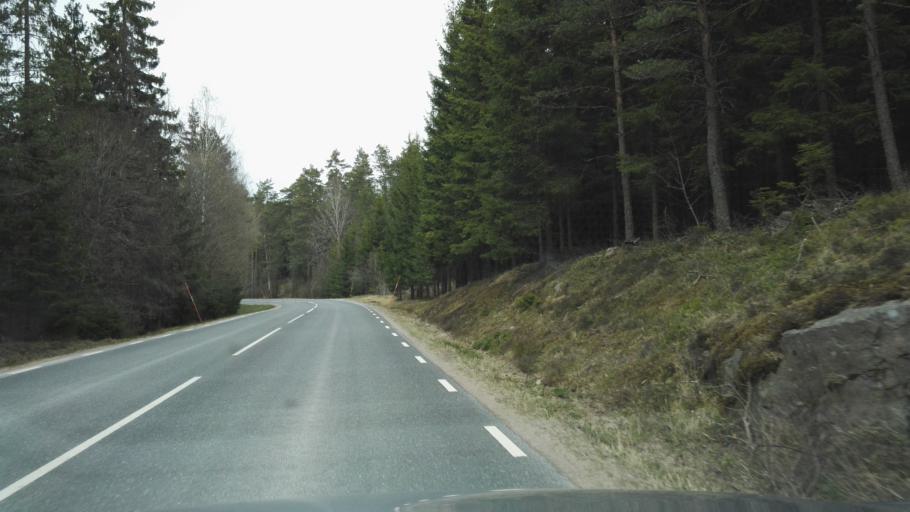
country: SE
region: Joenkoeping
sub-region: Vetlanda Kommun
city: Landsbro
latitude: 57.2614
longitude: 14.9349
